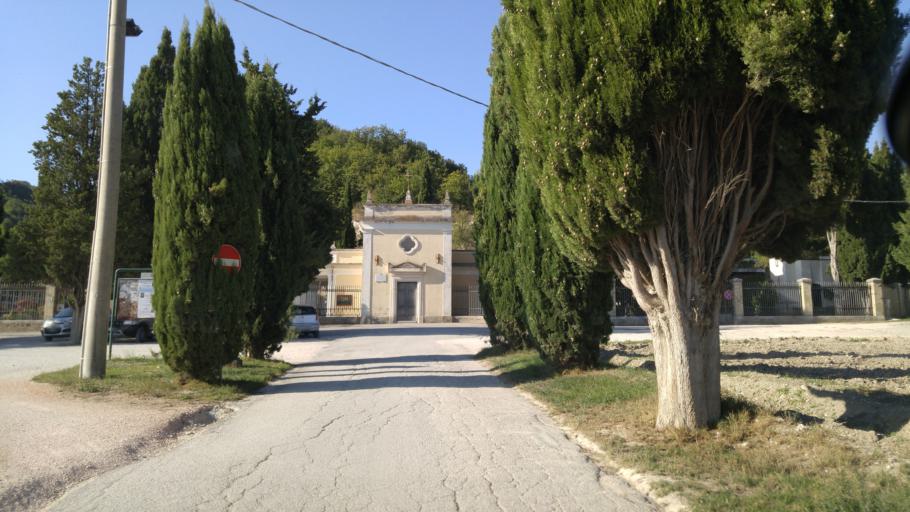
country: IT
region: The Marches
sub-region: Provincia di Pesaro e Urbino
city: Fermignano
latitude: 43.6722
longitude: 12.6341
